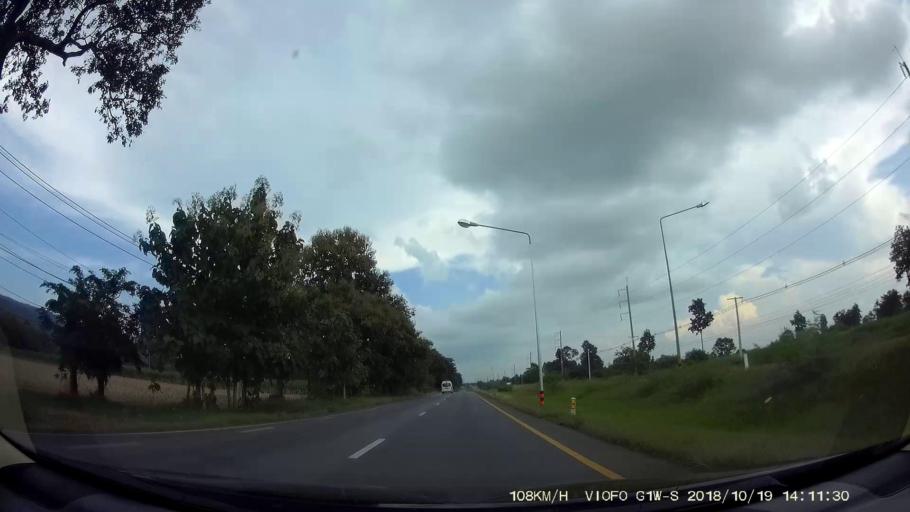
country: TH
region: Chaiyaphum
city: Khon Sawan
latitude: 15.9395
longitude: 102.1608
